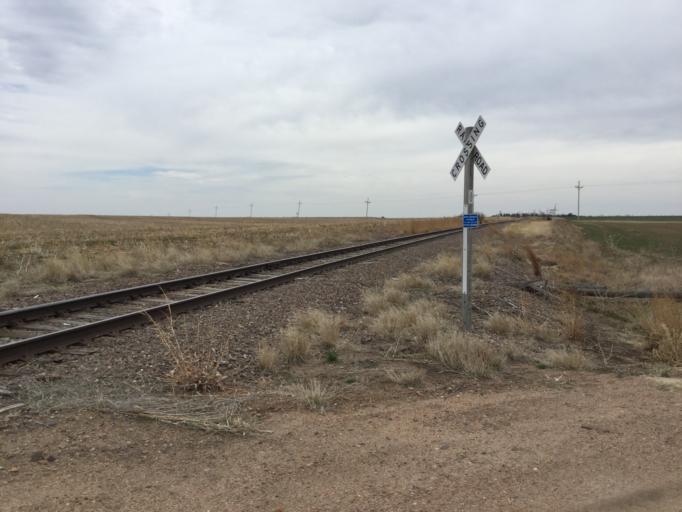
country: US
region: Kansas
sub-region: Barton County
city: Hoisington
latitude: 38.5083
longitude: -98.9041
